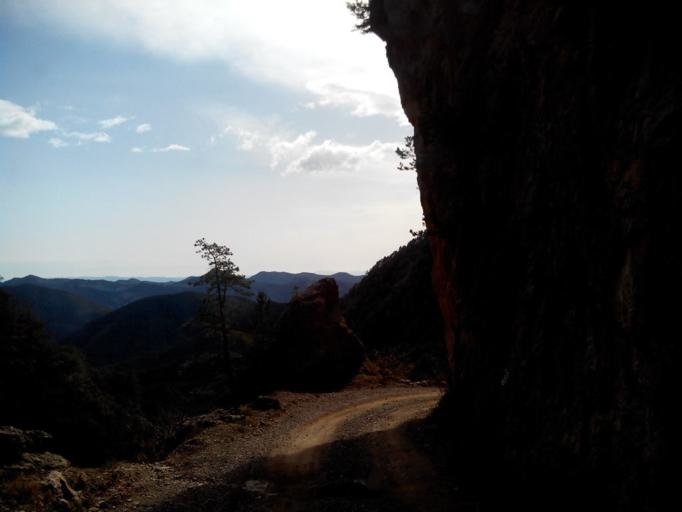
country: ES
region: Catalonia
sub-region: Provincia de Barcelona
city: Vilada
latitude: 42.1775
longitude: 1.9292
